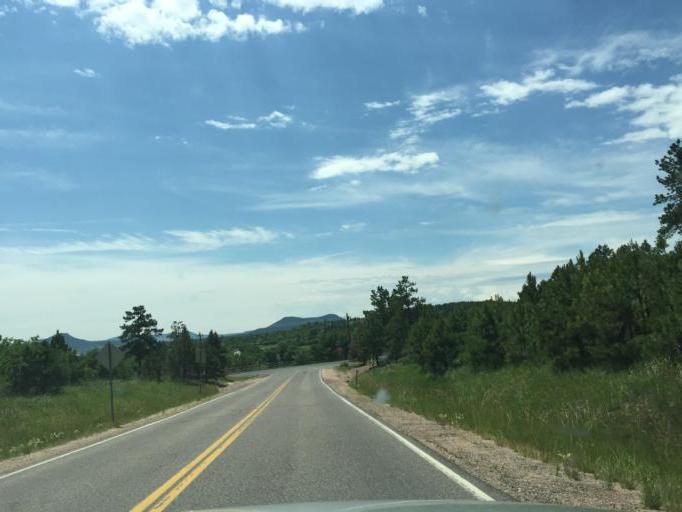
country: US
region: Colorado
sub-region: Douglas County
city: Perry Park
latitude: 39.2979
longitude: -104.9170
